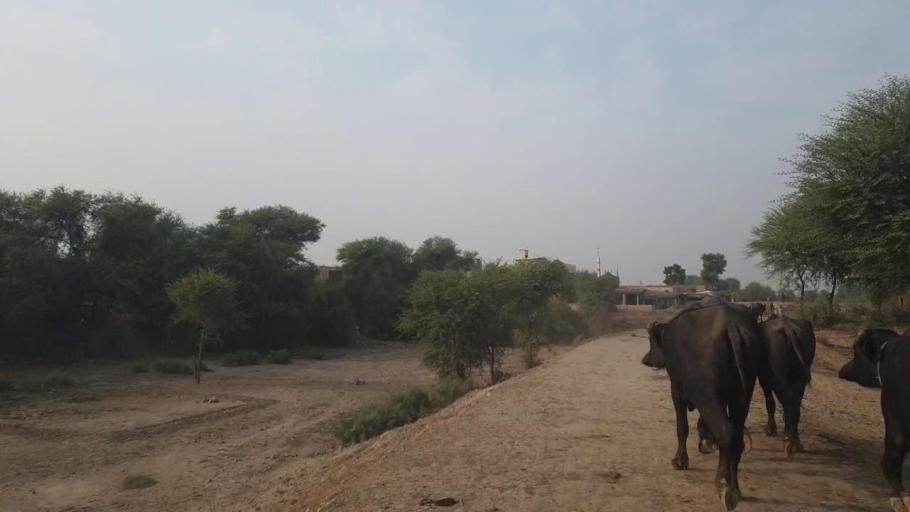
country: PK
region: Sindh
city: Sann
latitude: 26.0901
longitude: 68.0949
